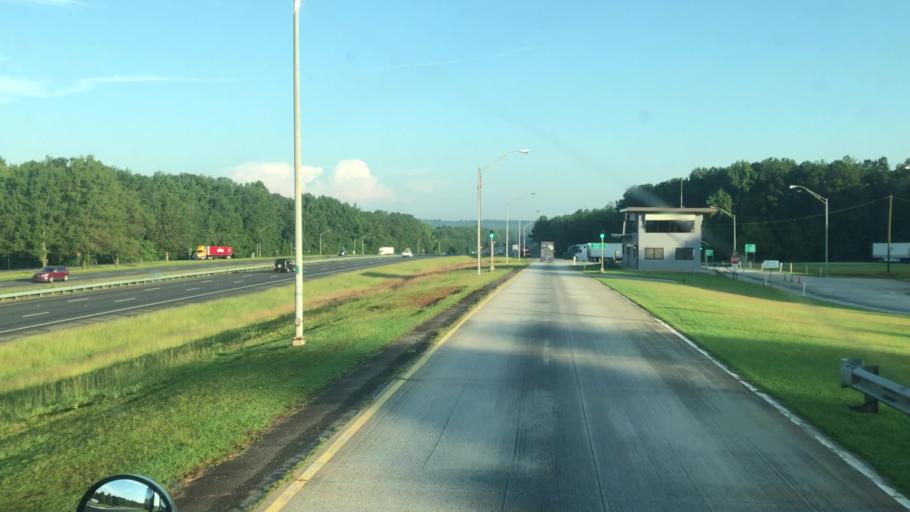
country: US
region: Georgia
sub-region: Monroe County
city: Forsyth
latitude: 33.0697
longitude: -83.9726
